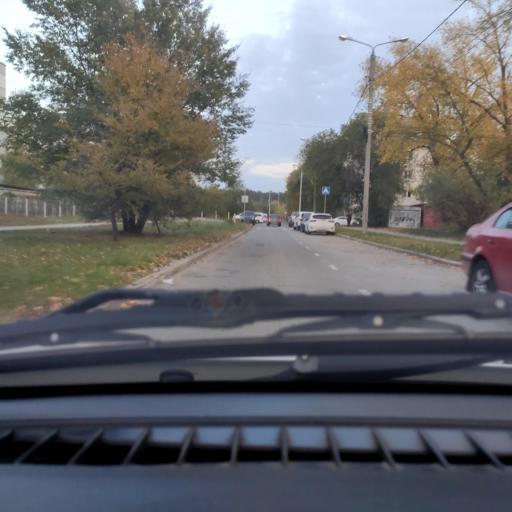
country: RU
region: Samara
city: Zhigulevsk
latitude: 53.4685
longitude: 49.5337
